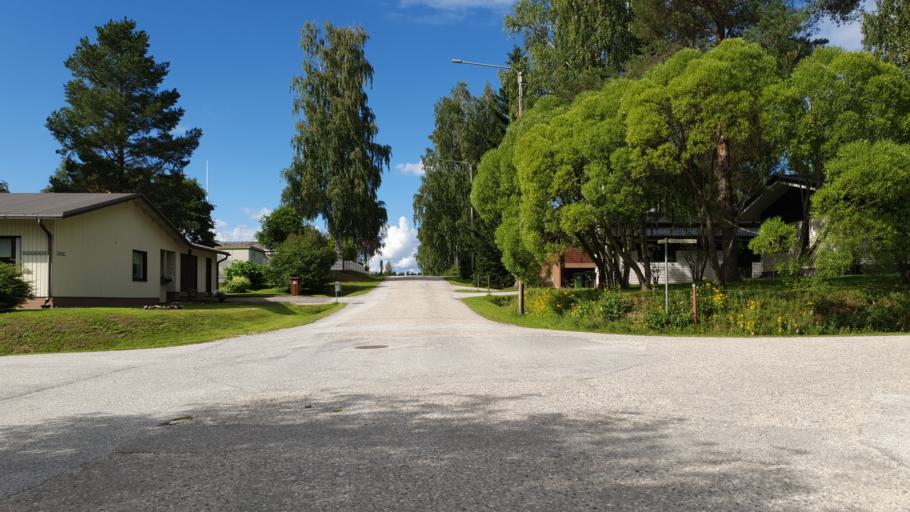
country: FI
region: Kainuu
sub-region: Kehys-Kainuu
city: Kuhmo
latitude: 64.1331
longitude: 29.5312
